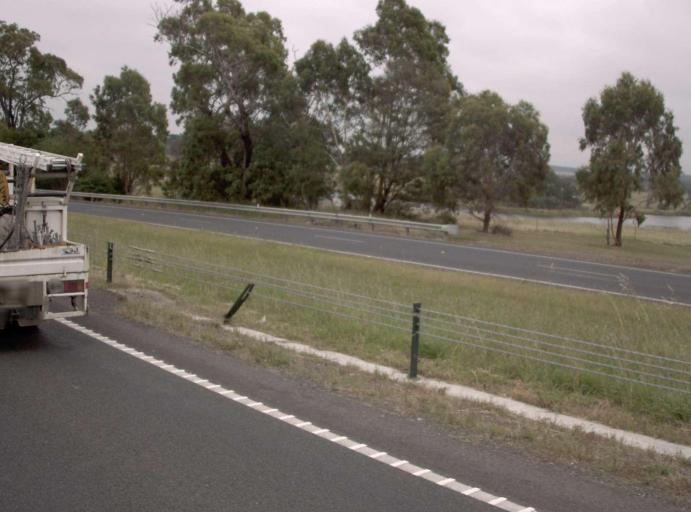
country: AU
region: Victoria
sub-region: Latrobe
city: Traralgon
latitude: -38.2103
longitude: 146.4901
